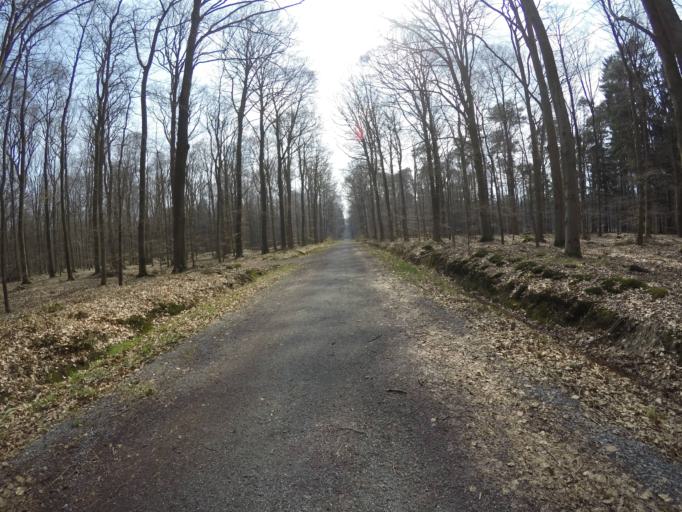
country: DE
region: Schleswig-Holstein
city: Ellerhoop
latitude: 53.7197
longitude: 9.7990
